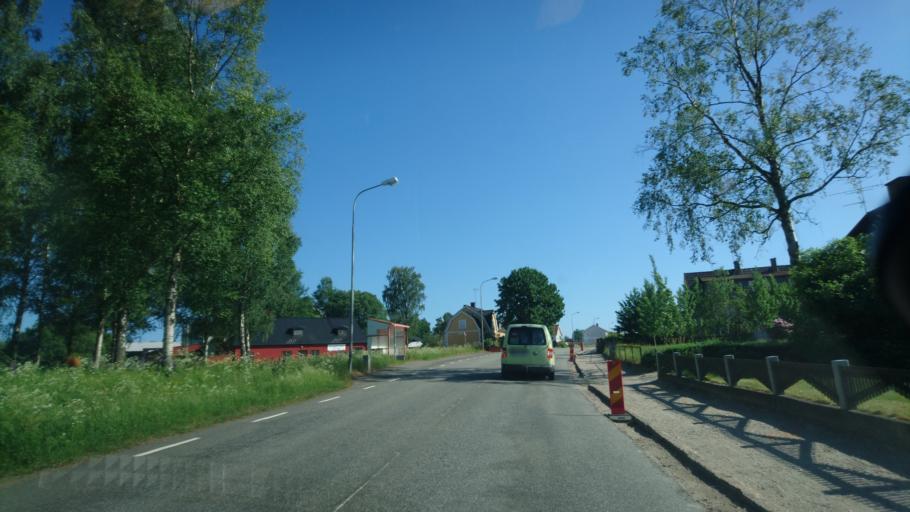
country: SE
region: Skane
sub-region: Osby Kommun
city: Lonsboda
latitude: 56.4028
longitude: 14.3192
